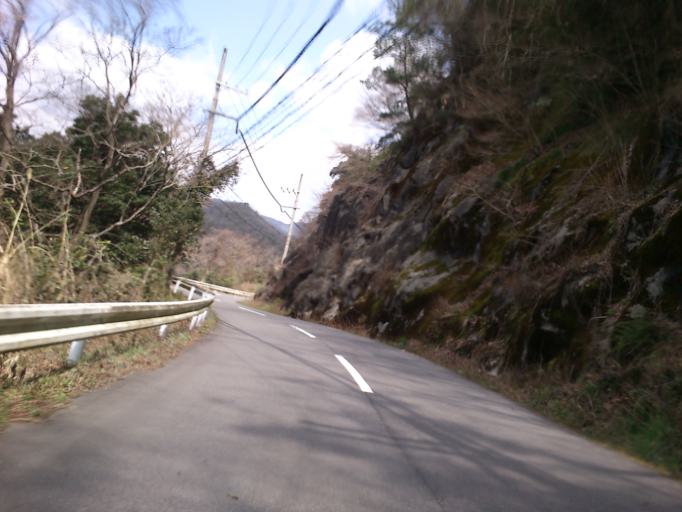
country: JP
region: Mie
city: Ueno-ebisumachi
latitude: 34.7609
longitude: 136.0051
